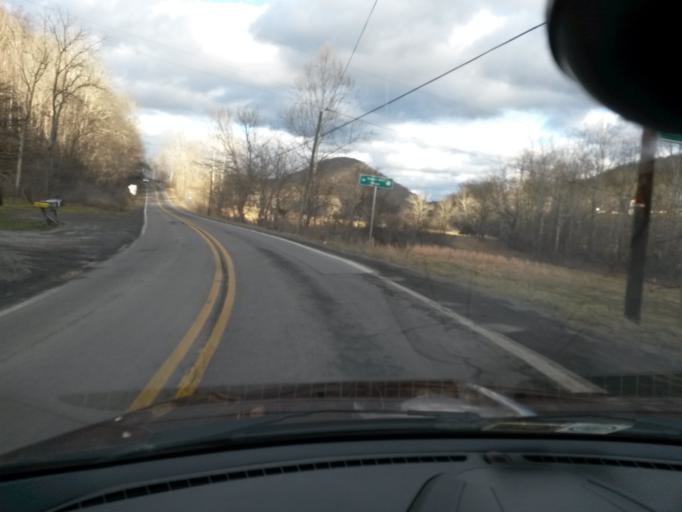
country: US
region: West Virginia
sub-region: Monroe County
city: Union
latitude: 37.5268
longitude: -80.6044
